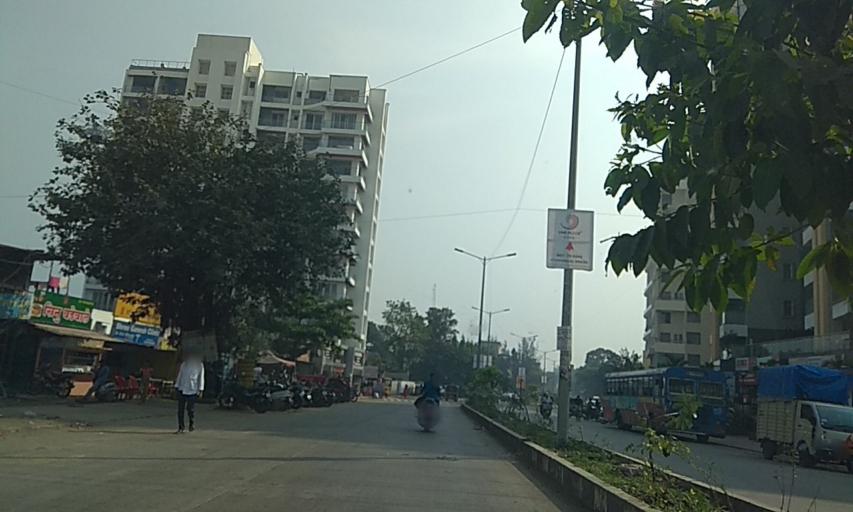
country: IN
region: Maharashtra
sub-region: Pune Division
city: Pimpri
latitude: 18.5598
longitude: 73.7805
